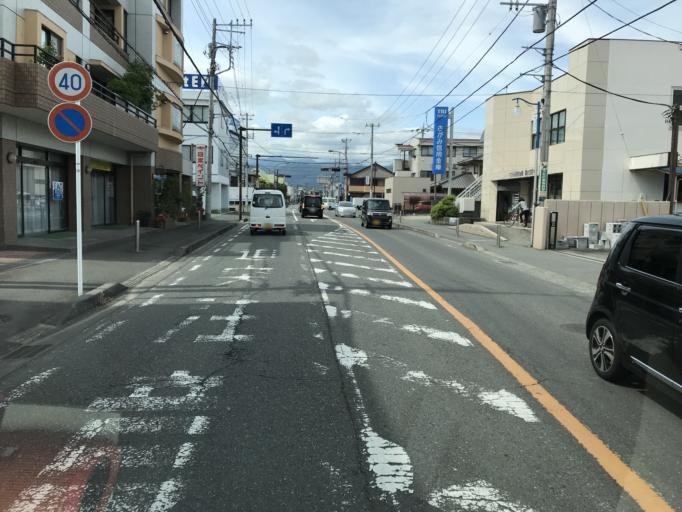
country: JP
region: Kanagawa
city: Odawara
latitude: 35.2944
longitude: 139.1482
